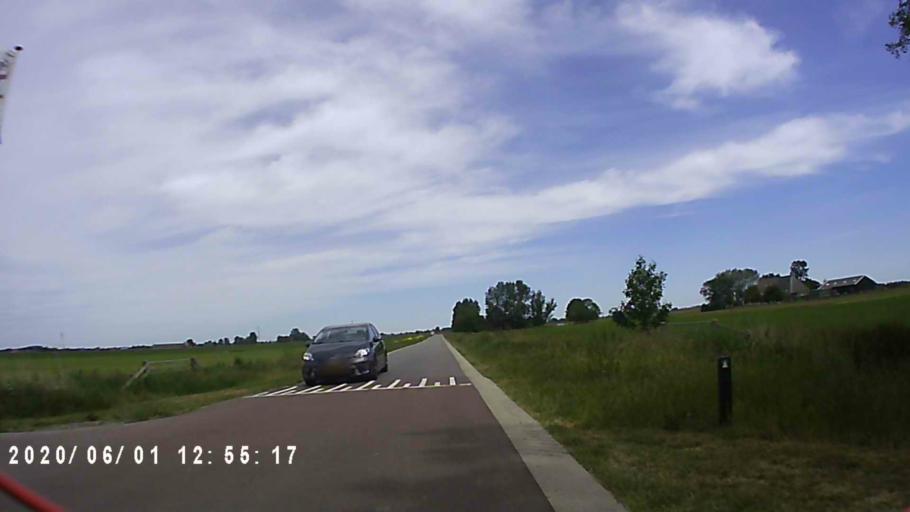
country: NL
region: Friesland
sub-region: Gemeente Franekeradeel
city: Tzum
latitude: 53.1423
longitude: 5.5214
